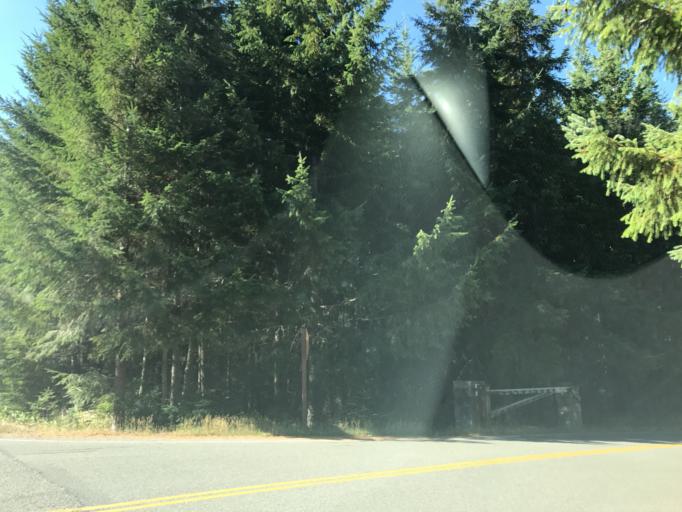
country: US
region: Washington
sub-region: King County
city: Riverbend
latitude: 47.0858
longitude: -121.5830
